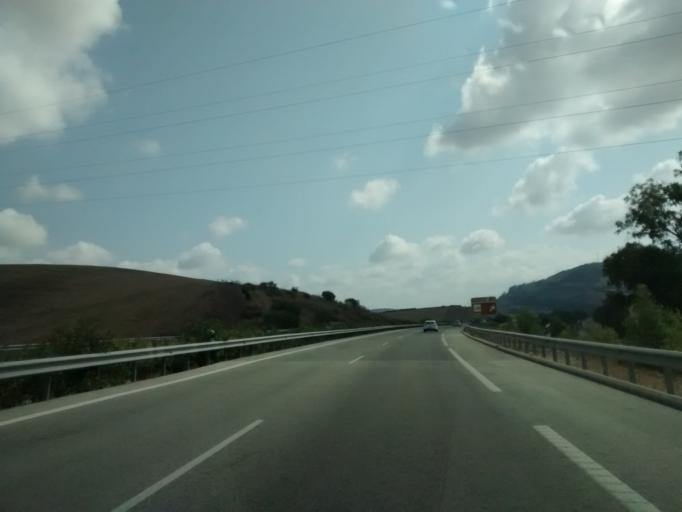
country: ES
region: Andalusia
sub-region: Provincia de Cadiz
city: Vejer de la Frontera
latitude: 36.2519
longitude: -6.0023
